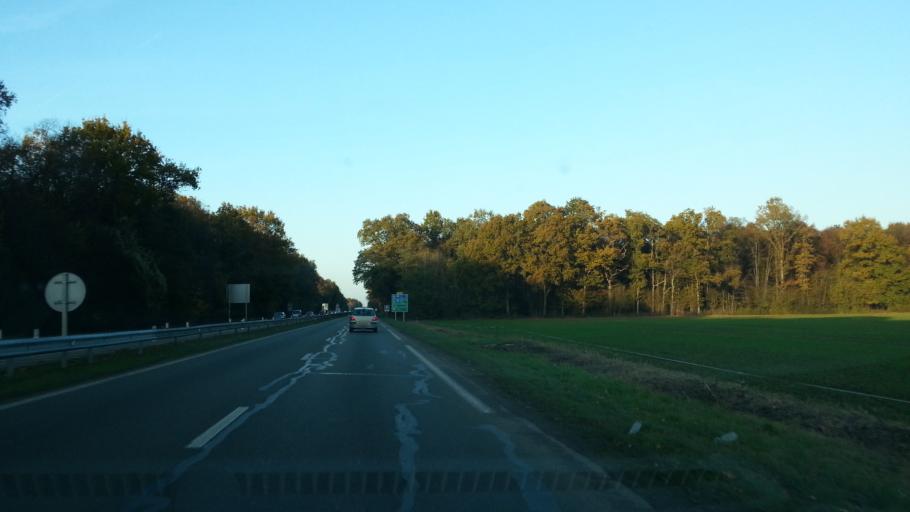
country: FR
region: Picardie
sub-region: Departement de l'Oise
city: Chantilly
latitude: 49.2074
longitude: 2.4628
